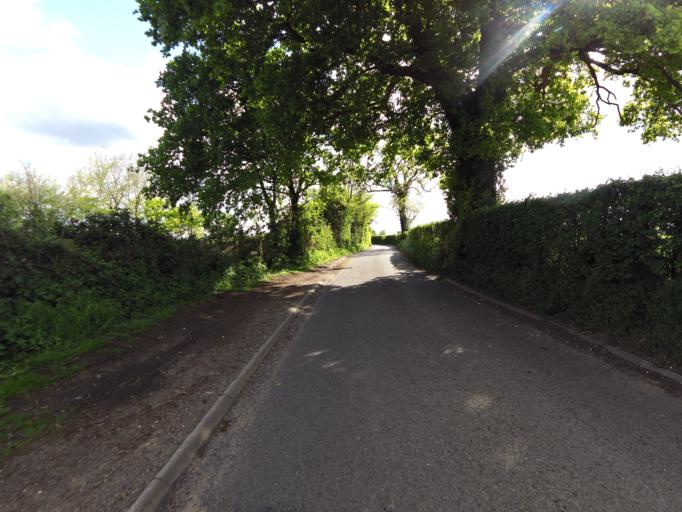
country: GB
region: England
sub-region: Suffolk
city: Woolpit
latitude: 52.2274
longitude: 0.8574
